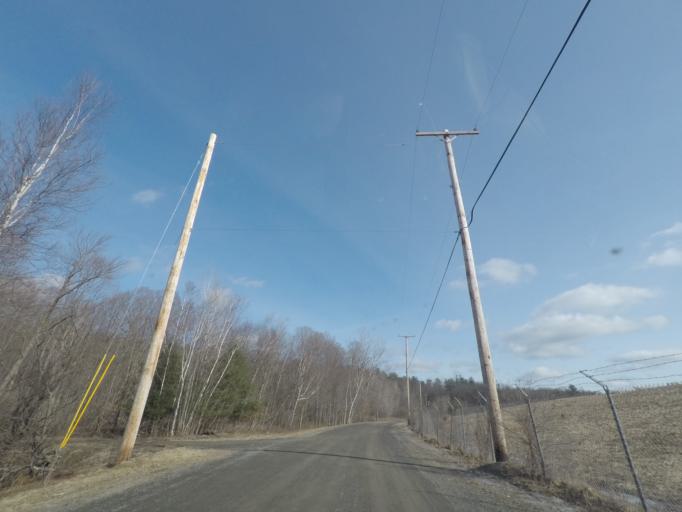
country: US
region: New York
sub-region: Rensselaer County
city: Nassau
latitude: 42.5609
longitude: -73.5634
